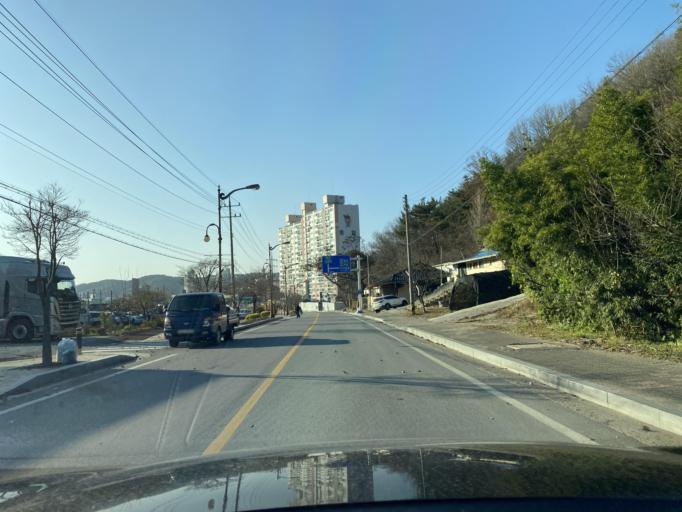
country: KR
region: Chungcheongnam-do
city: Yesan
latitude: 36.6809
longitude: 126.8572
